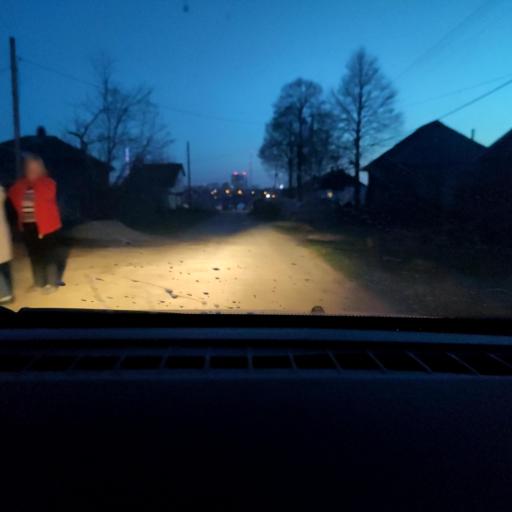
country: RU
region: Perm
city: Perm
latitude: 58.0234
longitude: 56.3257
